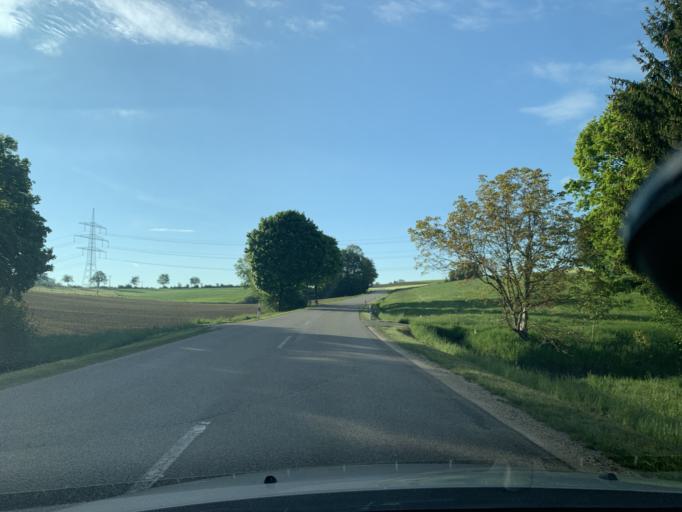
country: DE
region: Bavaria
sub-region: Lower Bavaria
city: Adlkofen
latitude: 48.5308
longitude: 12.2582
